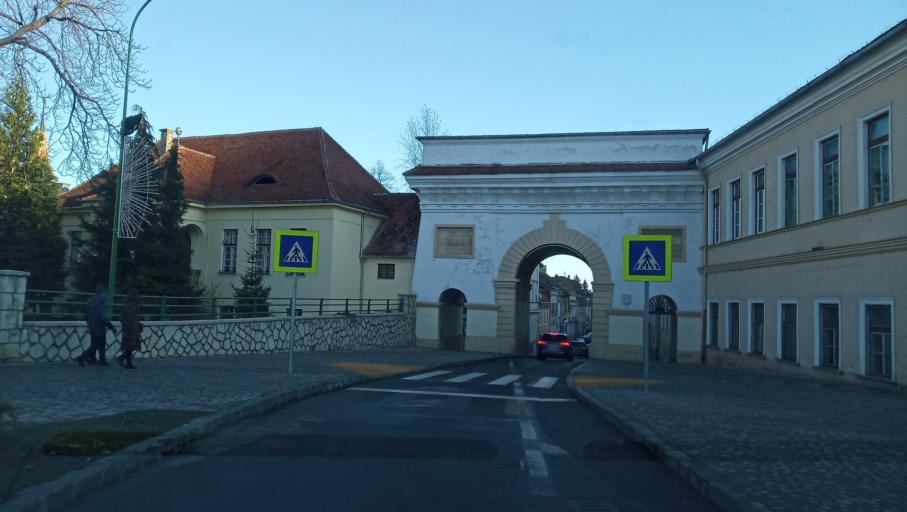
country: RO
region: Brasov
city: Brasov
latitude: 45.6389
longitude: 25.5860
